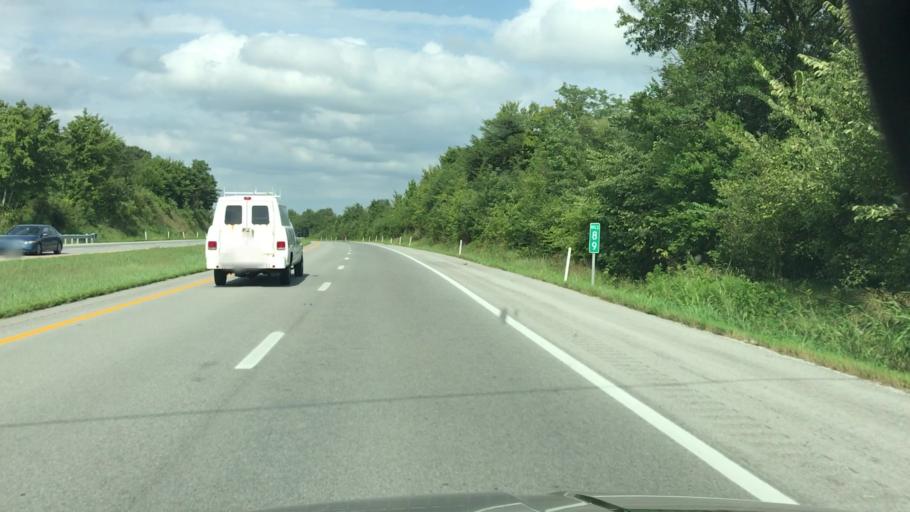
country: US
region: Kentucky
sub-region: Hopkins County
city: Dawson Springs
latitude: 37.1707
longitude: -87.7420
